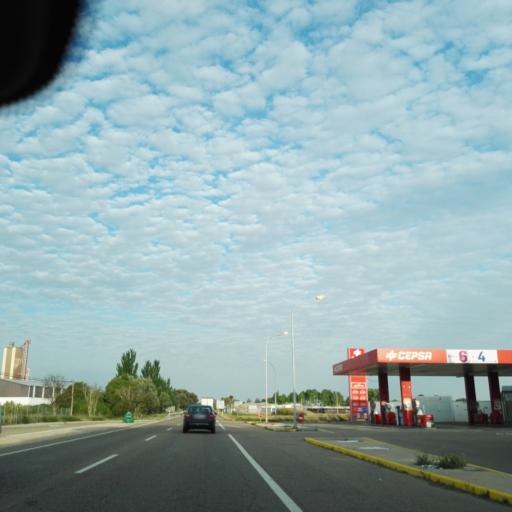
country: ES
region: Aragon
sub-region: Provincia de Zaragoza
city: Utebo
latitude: 41.6635
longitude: -0.9830
